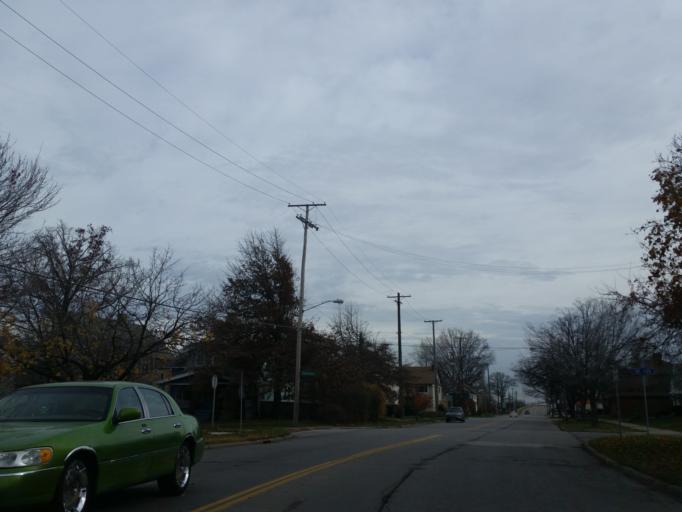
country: US
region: Ohio
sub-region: Cuyahoga County
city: Lakewood
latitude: 41.4704
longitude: -81.7891
